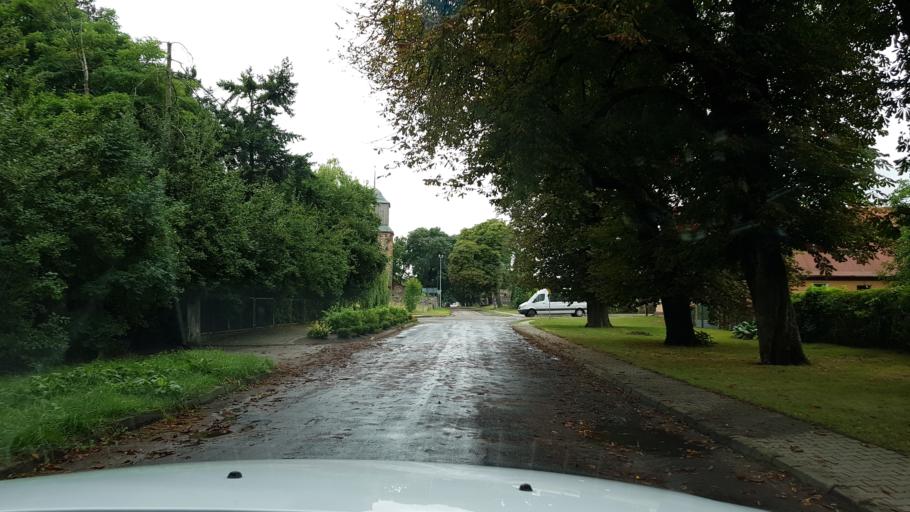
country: PL
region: West Pomeranian Voivodeship
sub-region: Powiat pyrzycki
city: Przelewice
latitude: 53.1103
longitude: 15.1054
